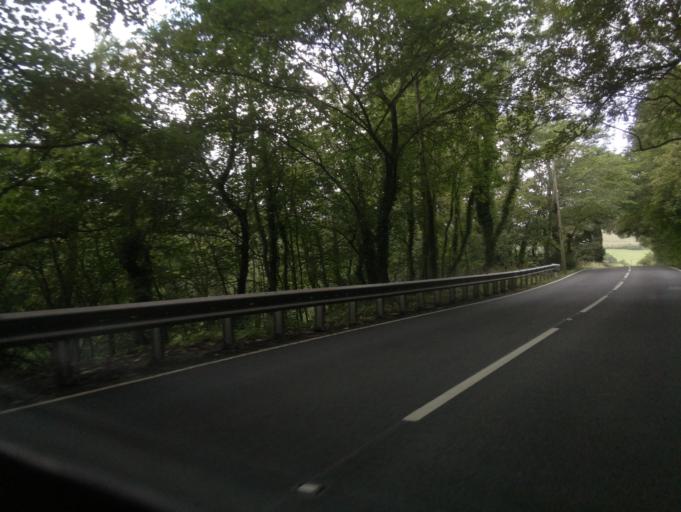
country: GB
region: England
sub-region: North Yorkshire
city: Leyburn
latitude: 54.4005
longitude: -1.8238
